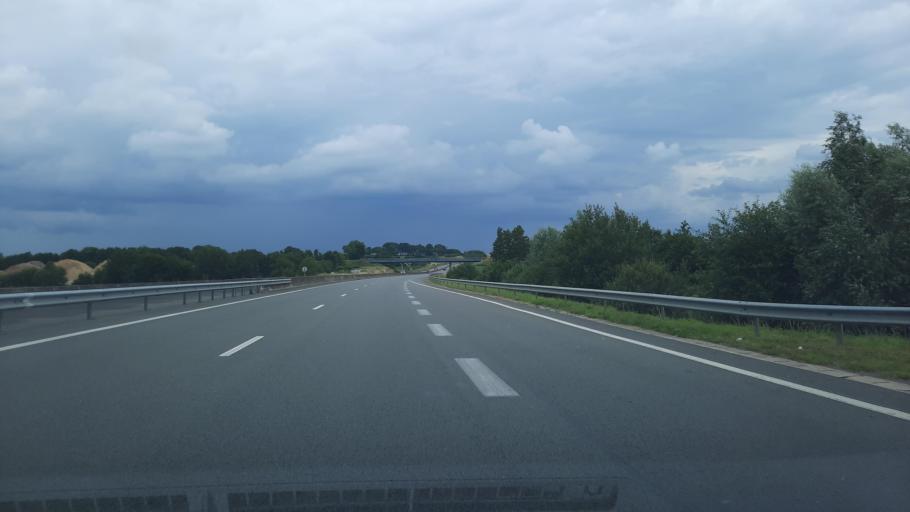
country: FR
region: Nord-Pas-de-Calais
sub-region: Departement du Nord
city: Hautmont
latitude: 50.2083
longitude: 3.9546
